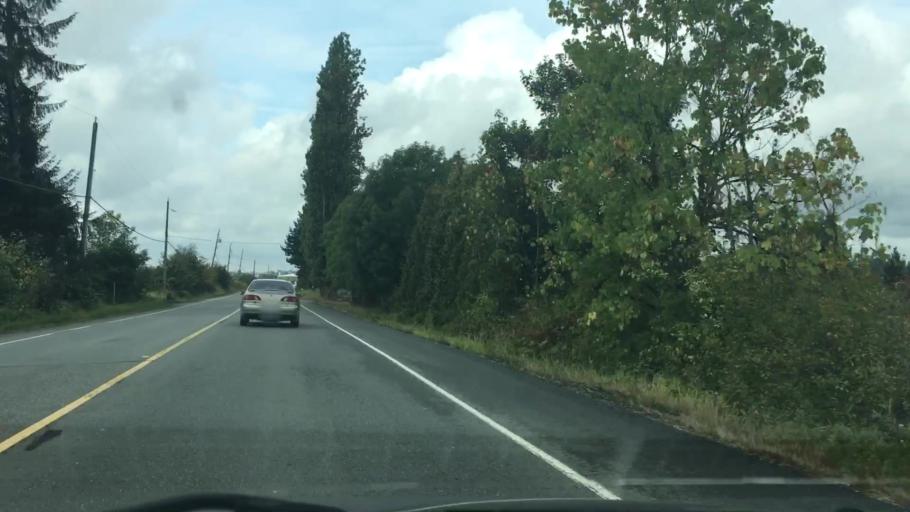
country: CA
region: British Columbia
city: Langley
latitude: 49.1042
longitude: -122.6120
